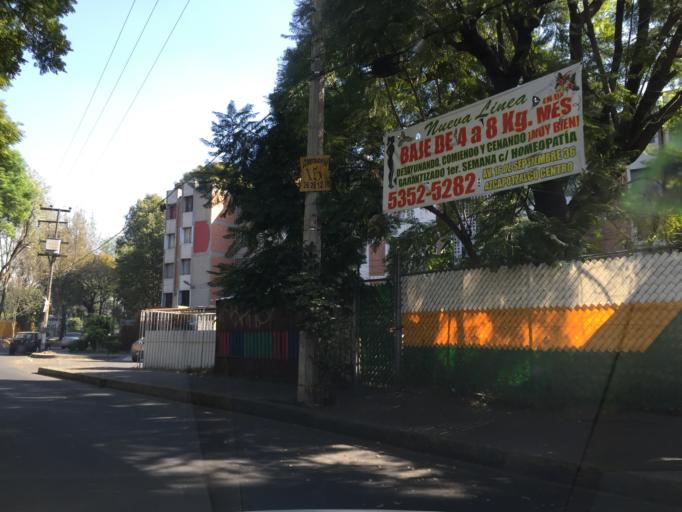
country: MX
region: Mexico City
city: Azcapotzalco
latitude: 19.4982
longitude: -99.2030
